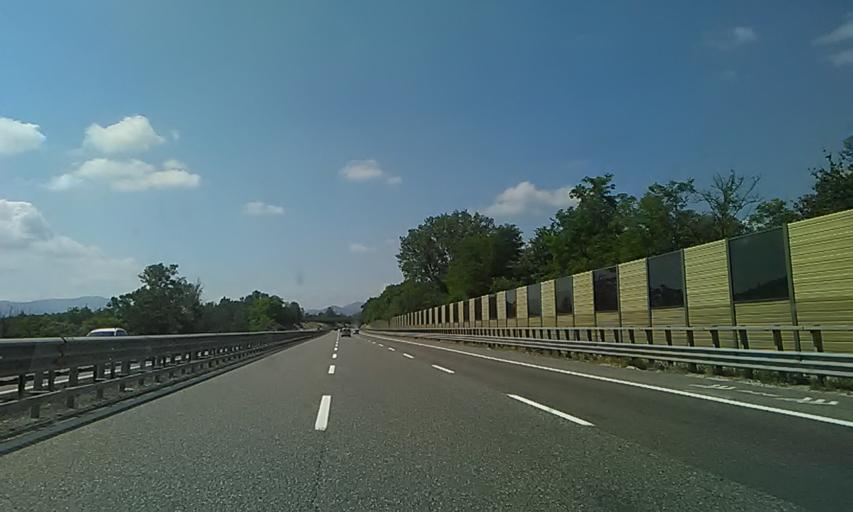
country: IT
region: Piedmont
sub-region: Provincia di Alessandria
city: Silvano d'Orba
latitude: 44.6953
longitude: 8.6661
